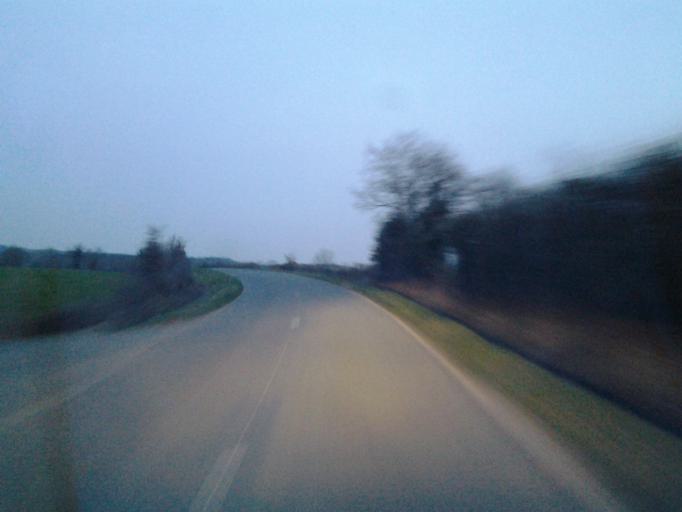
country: FR
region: Pays de la Loire
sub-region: Departement de la Vendee
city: Saint-Florent-des-Bois
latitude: 46.5780
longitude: -1.3493
